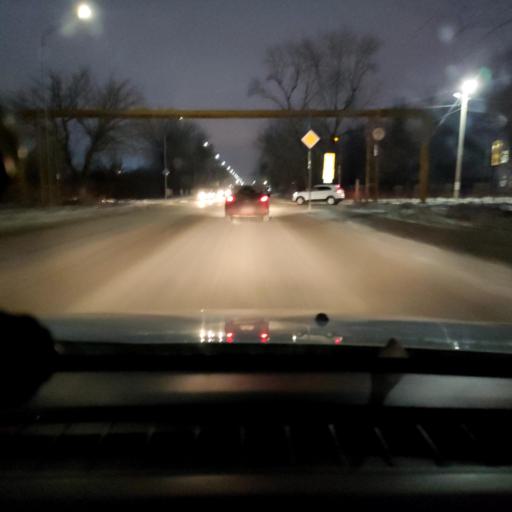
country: RU
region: Samara
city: Chapayevsk
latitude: 52.9731
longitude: 49.7011
